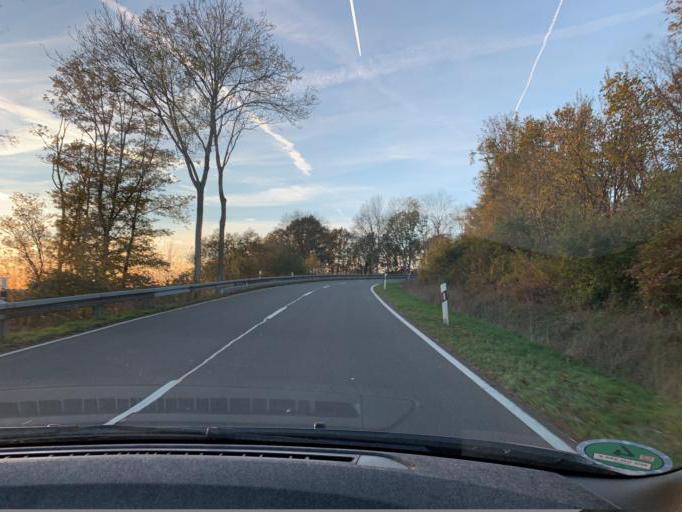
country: DE
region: North Rhine-Westphalia
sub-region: Regierungsbezirk Koln
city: Simmerath
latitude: 50.5896
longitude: 6.3663
